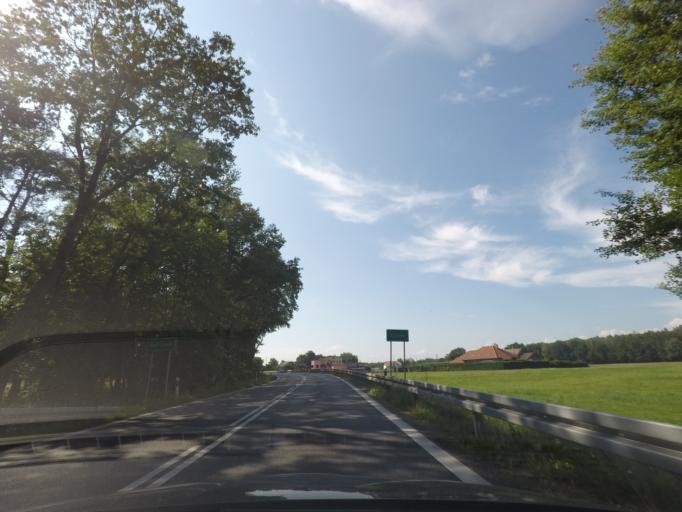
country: PL
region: Silesian Voivodeship
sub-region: Powiat pszczynski
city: Kryry
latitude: 50.0255
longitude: 18.8365
